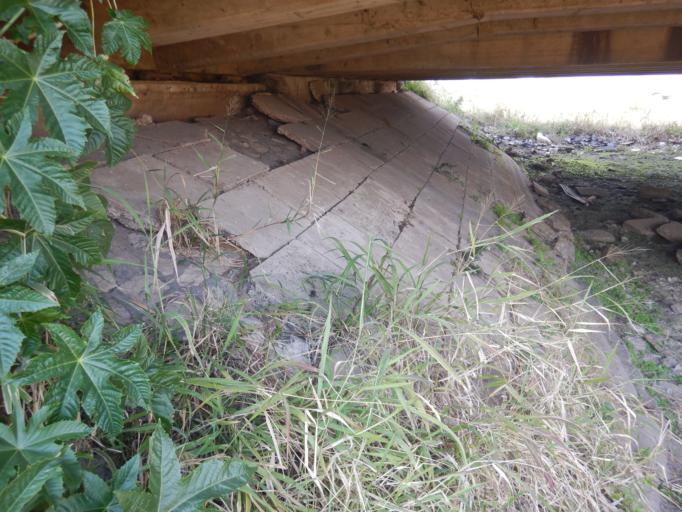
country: AR
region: Santa Fe
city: Santa Fe de la Vera Cruz
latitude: -31.6404
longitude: -60.6651
